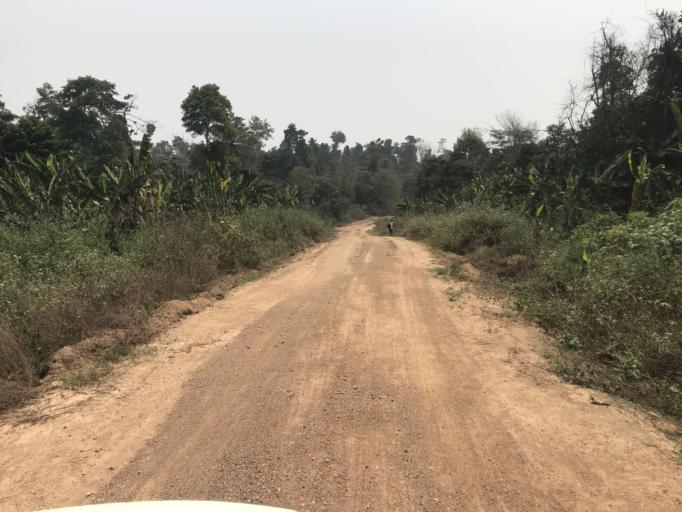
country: NG
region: Osun
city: Ifetedo
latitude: 7.0505
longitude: 4.4767
